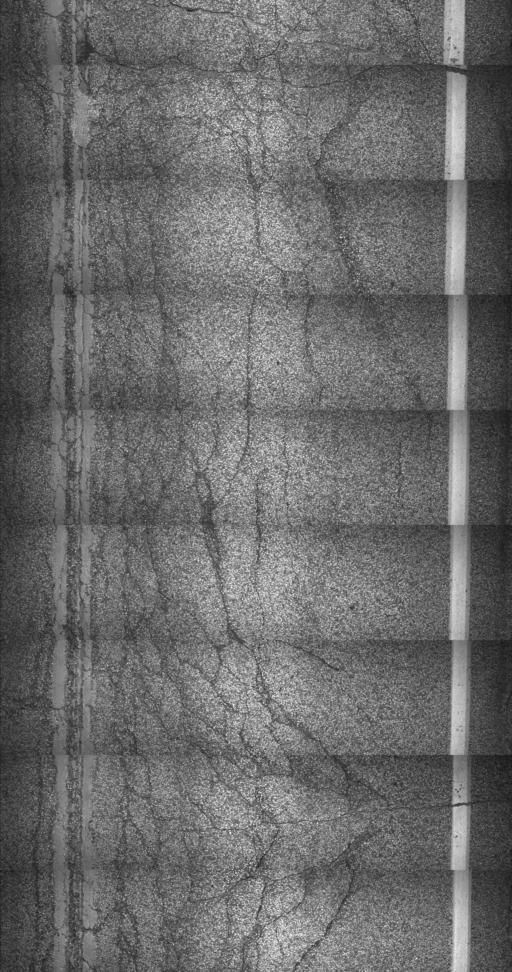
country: US
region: Vermont
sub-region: Washington County
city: Northfield
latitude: 44.0778
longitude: -72.7383
